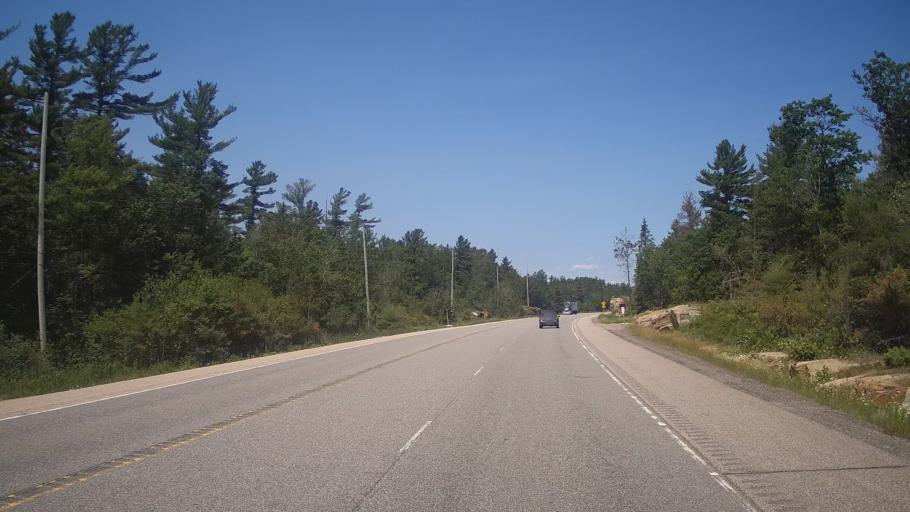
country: CA
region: Ontario
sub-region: Parry Sound District
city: Parry Sound
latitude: 45.6274
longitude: -80.3929
